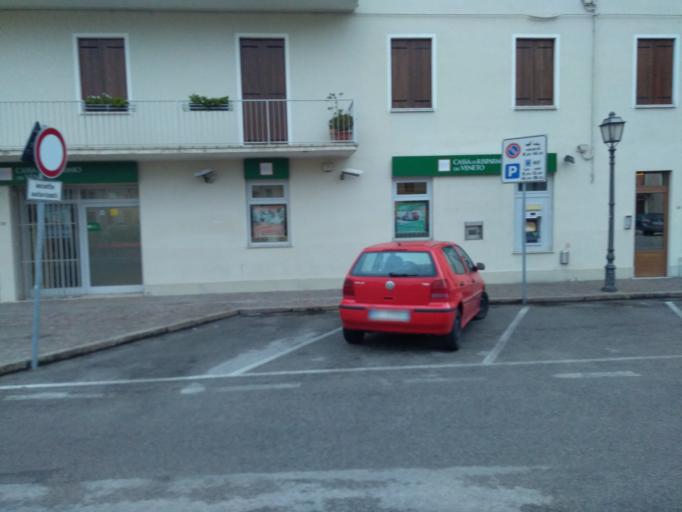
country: IT
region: Veneto
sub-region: Provincia di Vicenza
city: Isola Vicentina
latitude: 45.6291
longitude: 11.4429
